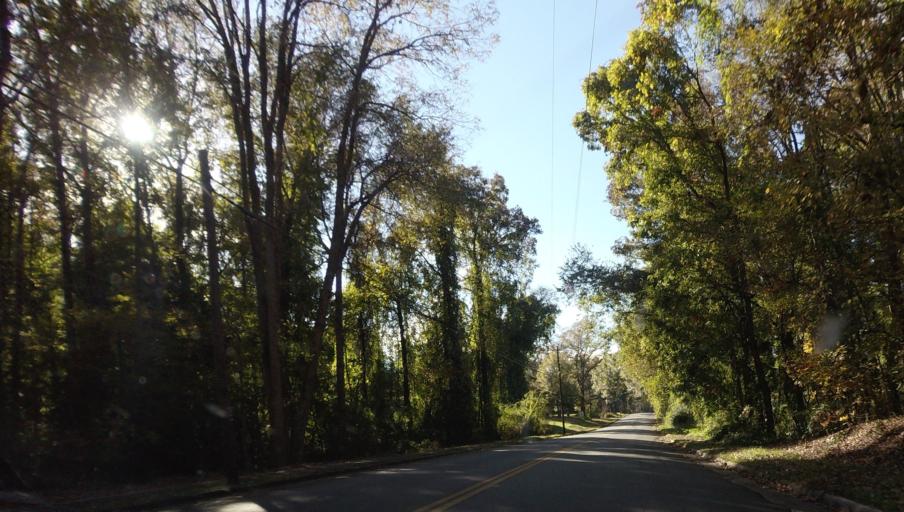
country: US
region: Georgia
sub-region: Talbot County
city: Talbotton
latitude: 32.6777
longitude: -84.5495
